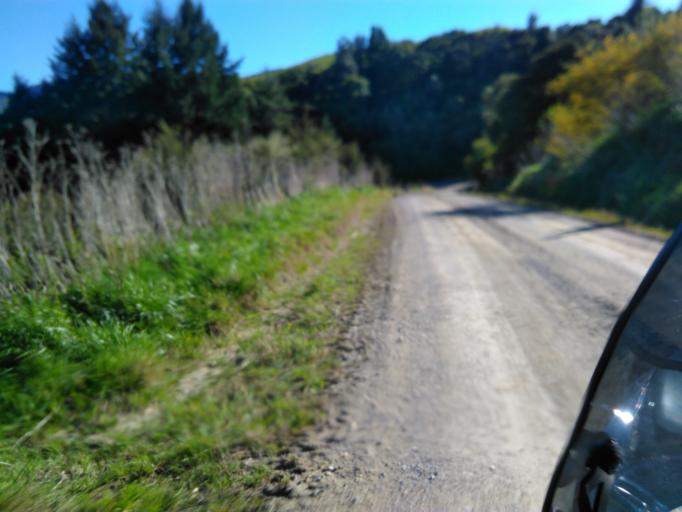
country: NZ
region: Gisborne
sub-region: Gisborne District
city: Gisborne
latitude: -38.3938
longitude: 177.6681
